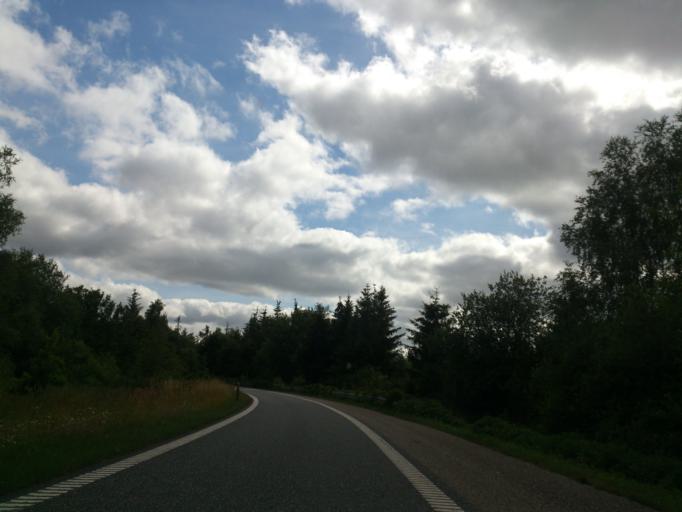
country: DK
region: South Denmark
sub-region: Aabenraa Kommune
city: Krusa
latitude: 54.8781
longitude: 9.3768
